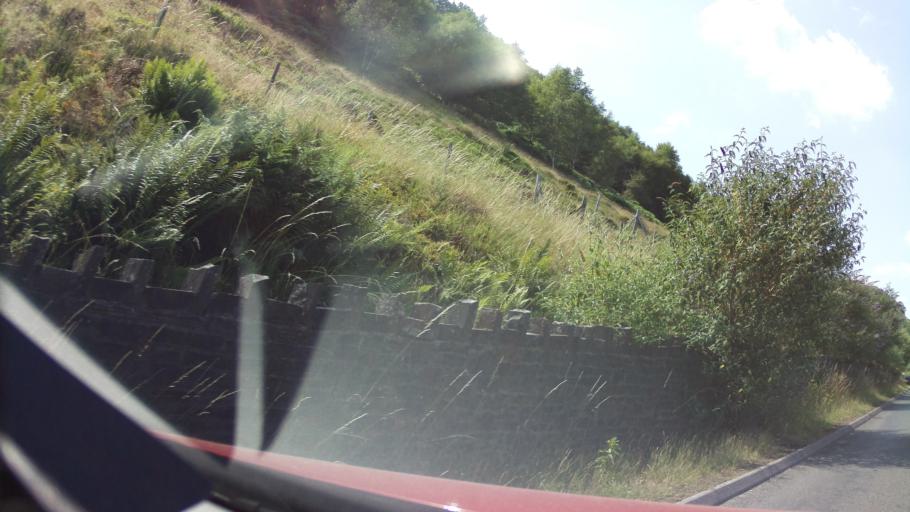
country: GB
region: Wales
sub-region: Caerphilly County Borough
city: New Tredegar
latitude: 51.7239
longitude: -3.2518
